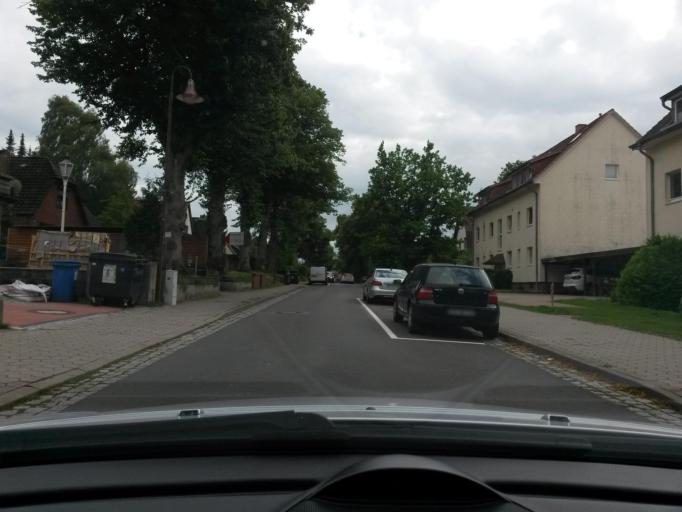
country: DE
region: Schleswig-Holstein
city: Glinde
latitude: 53.5458
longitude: 10.2123
